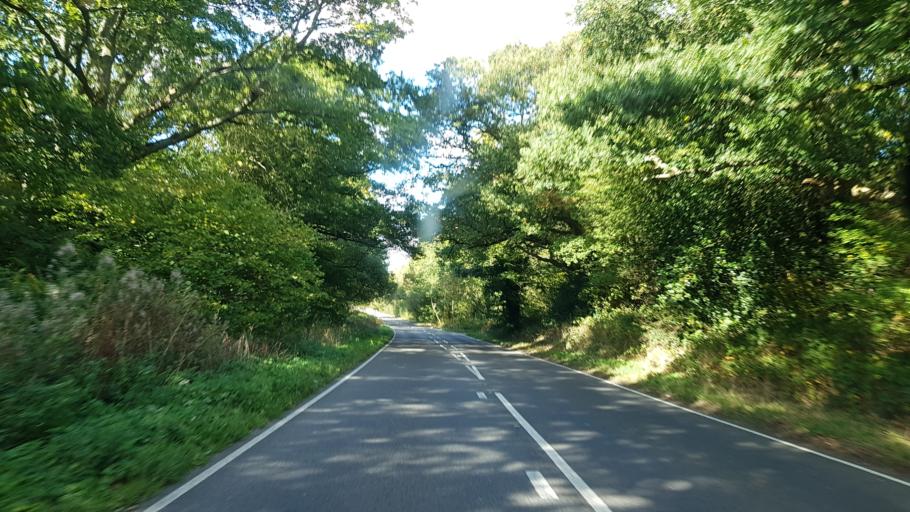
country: GB
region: England
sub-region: West Sussex
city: Petworth
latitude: 51.0235
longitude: -0.6241
